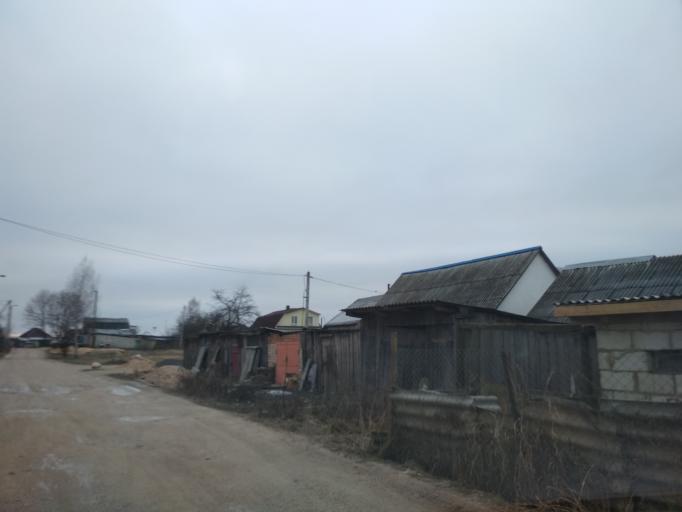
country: BY
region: Minsk
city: Mar''ina Horka
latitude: 53.5039
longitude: 28.1529
